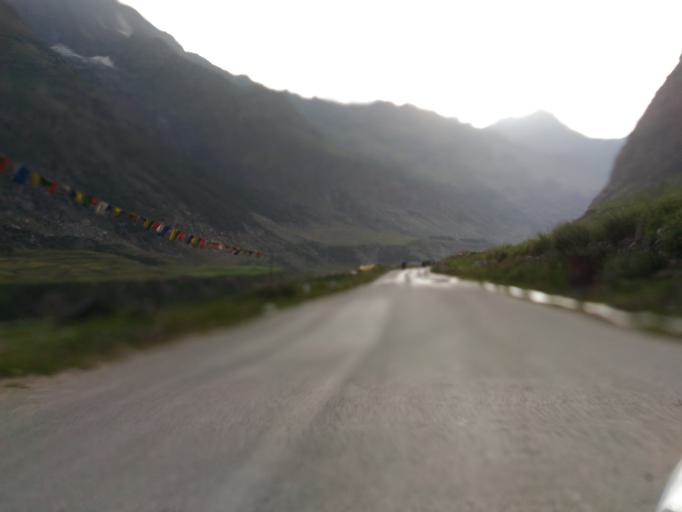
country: IN
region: Himachal Pradesh
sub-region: Kulu
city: Manali
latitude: 32.4347
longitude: 77.1893
